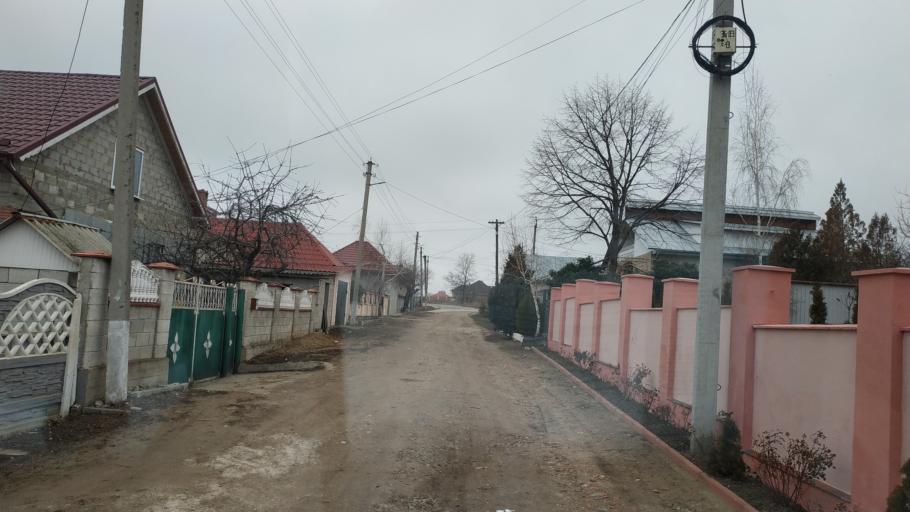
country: MD
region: Laloveni
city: Ialoveni
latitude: 46.8897
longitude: 28.6911
